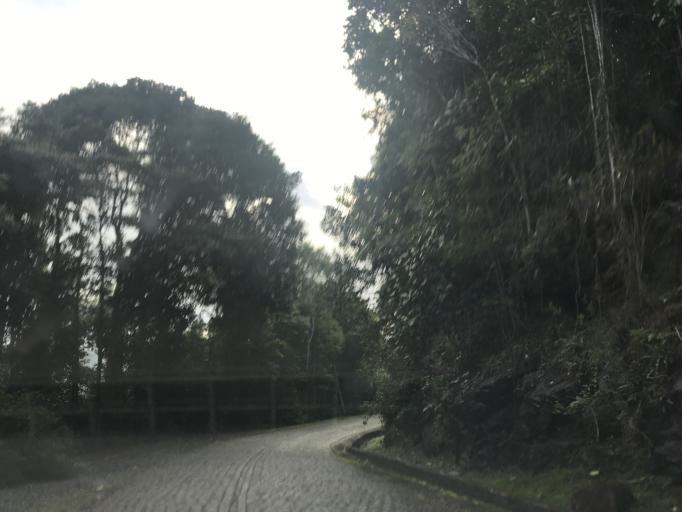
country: BR
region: Bahia
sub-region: Gandu
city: Gandu
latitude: -13.9061
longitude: -39.4681
